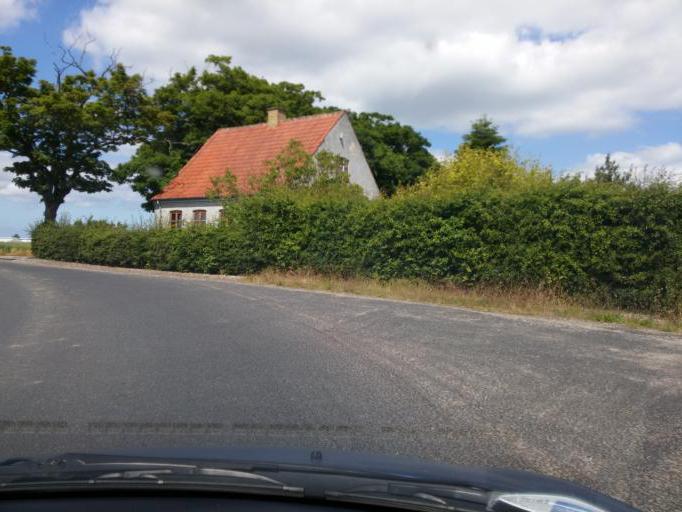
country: DK
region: South Denmark
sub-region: Kerteminde Kommune
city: Langeskov
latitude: 55.4085
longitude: 10.5825
